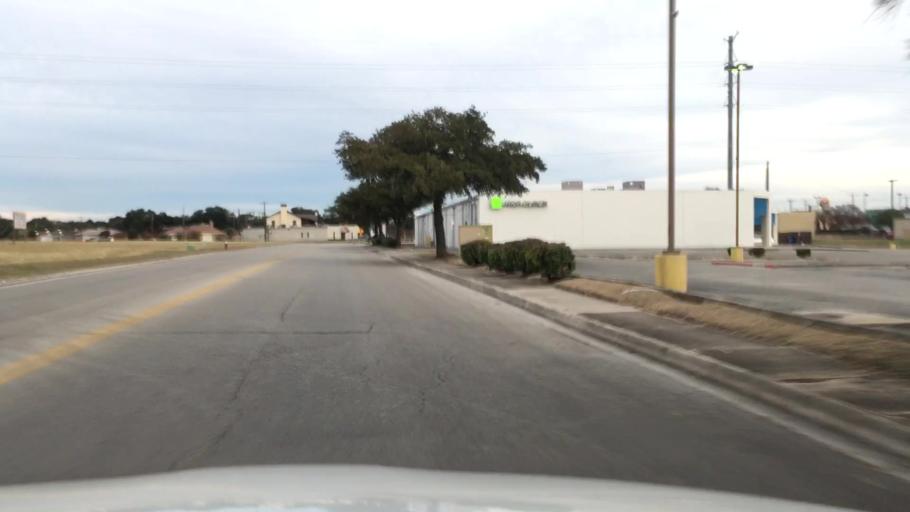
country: US
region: Texas
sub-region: Bexar County
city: Windcrest
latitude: 29.5118
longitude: -98.3927
